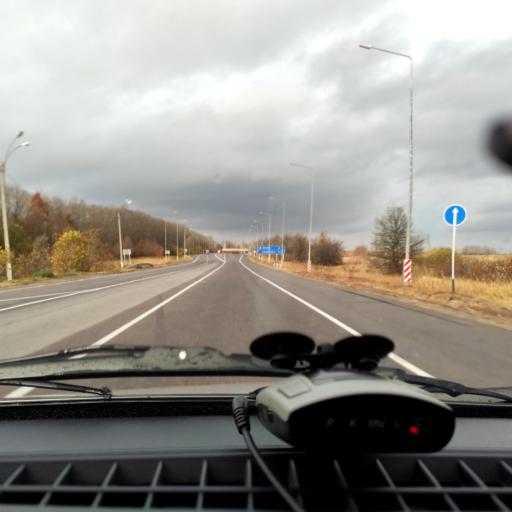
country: RU
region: Voronezj
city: Kolodeznyy
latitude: 51.3337
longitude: 39.0254
